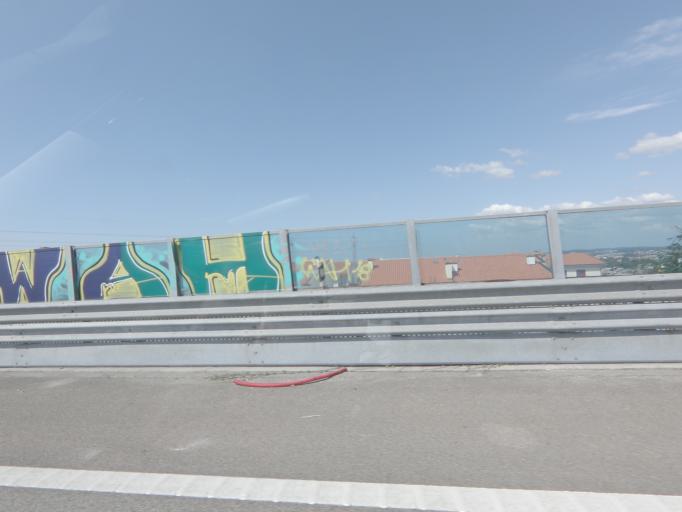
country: PT
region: Porto
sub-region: Matosinhos
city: Senhora da Hora
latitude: 41.2038
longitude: -8.6439
